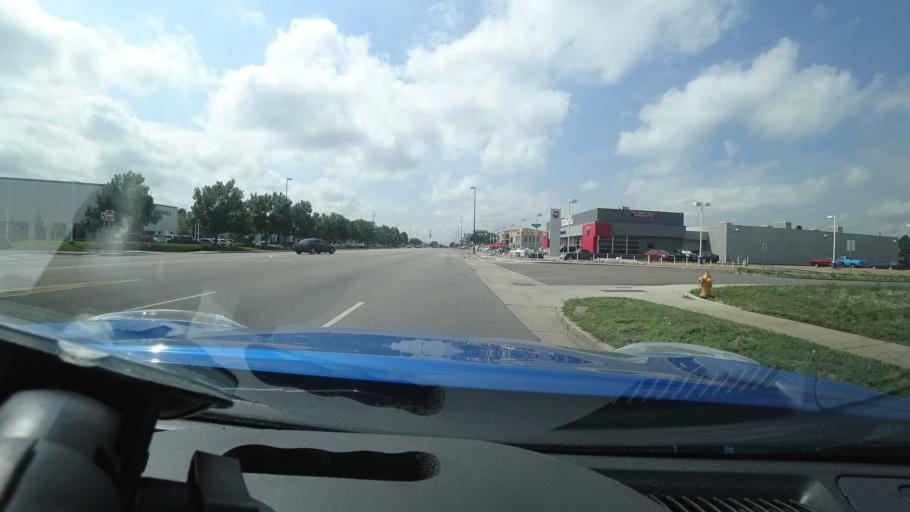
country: US
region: Colorado
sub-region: Adams County
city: Aurora
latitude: 39.7077
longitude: -104.8661
